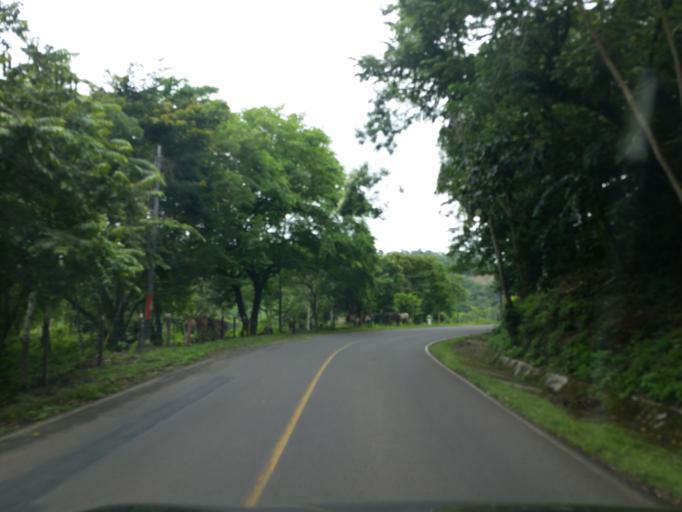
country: NI
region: Matagalpa
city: San Ramon
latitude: 13.0064
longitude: -85.8002
